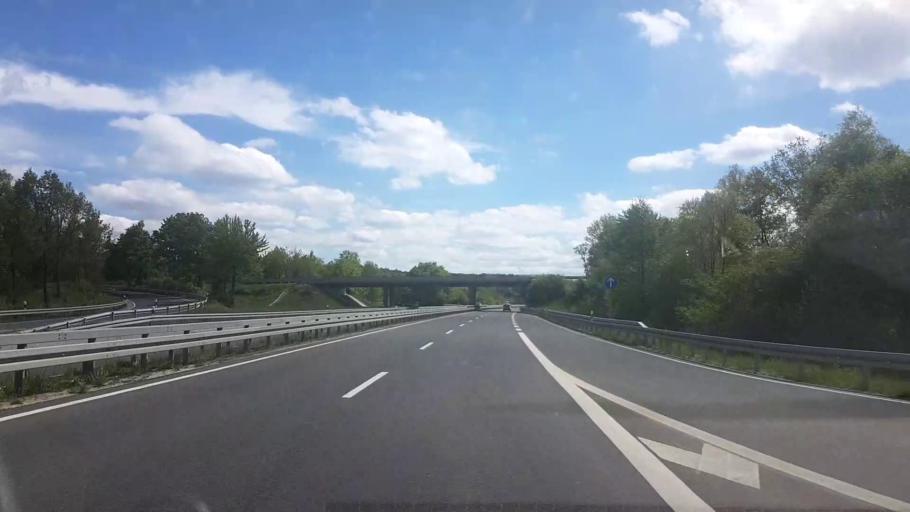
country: DE
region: Bavaria
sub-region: Upper Franconia
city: Niederfullbach
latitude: 50.2245
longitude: 10.9805
